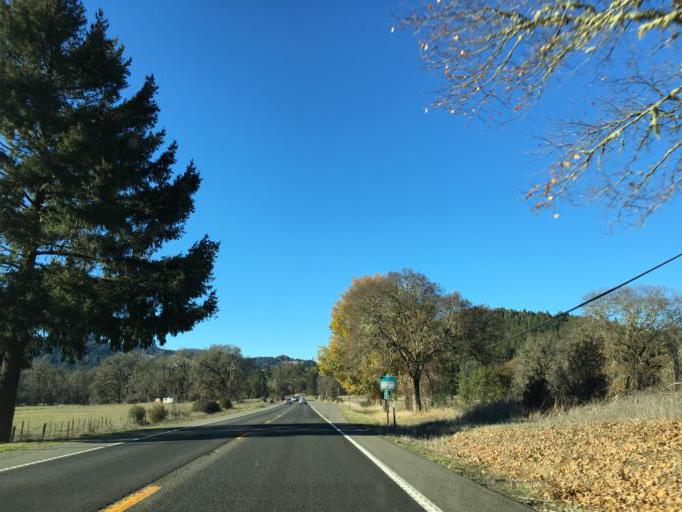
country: US
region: California
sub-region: Mendocino County
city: Laytonville
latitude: 39.7443
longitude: -123.5215
